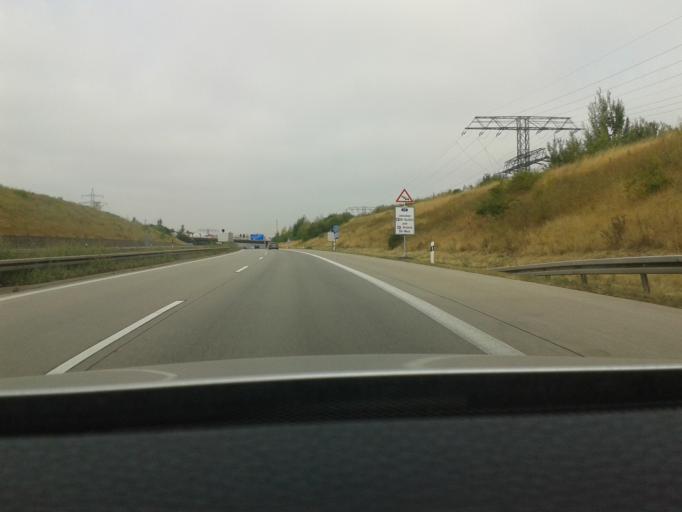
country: DE
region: Saxony
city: Bannewitz
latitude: 51.0067
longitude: 13.7359
